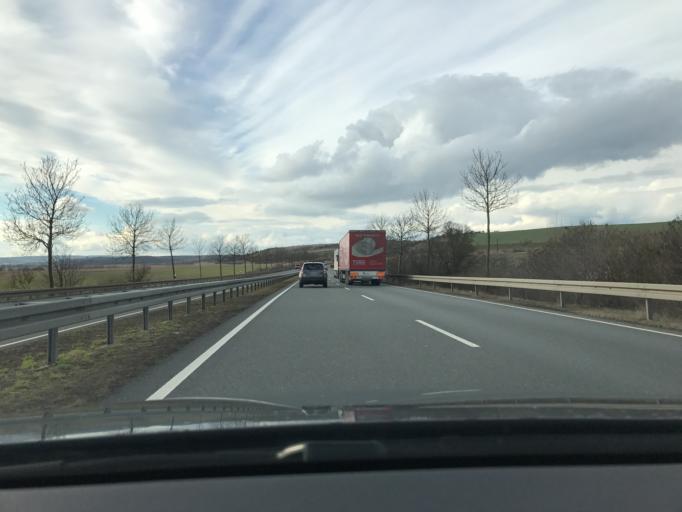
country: DE
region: Saxony-Anhalt
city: Hohnstedt
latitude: 51.4755
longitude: 11.7191
